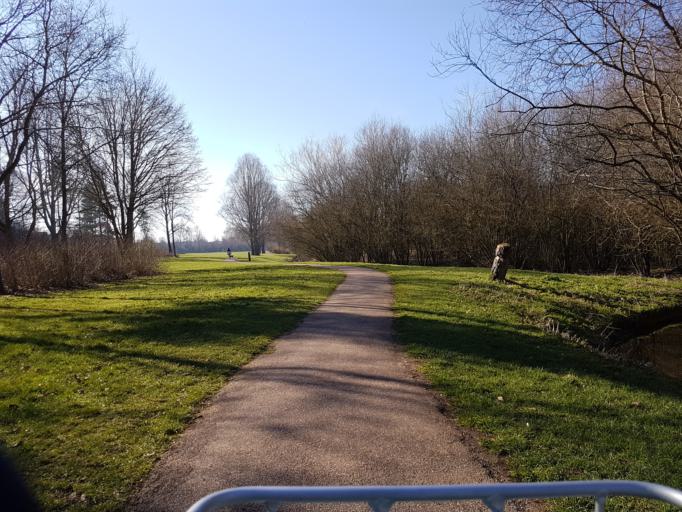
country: GB
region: England
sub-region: Milton Keynes
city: Loughton
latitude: 52.0104
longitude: -0.7617
